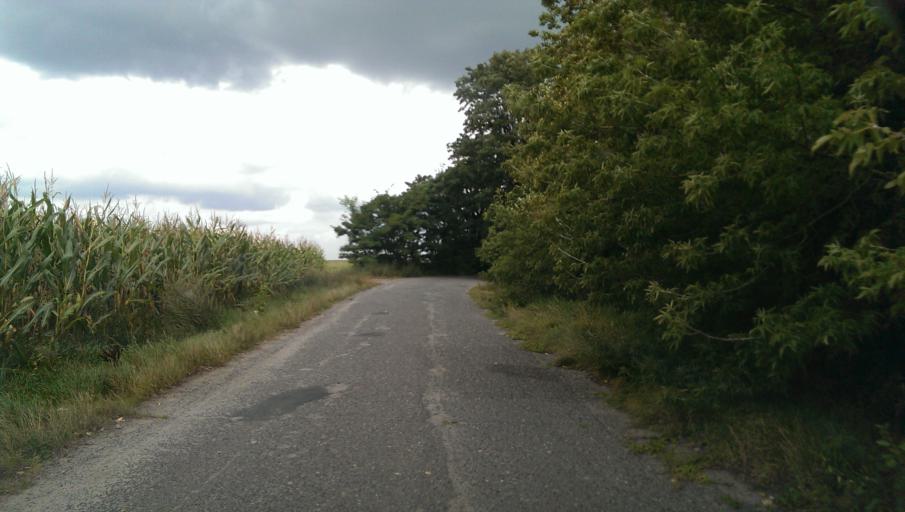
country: DE
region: Brandenburg
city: Rangsdorf
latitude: 52.2974
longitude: 13.4761
